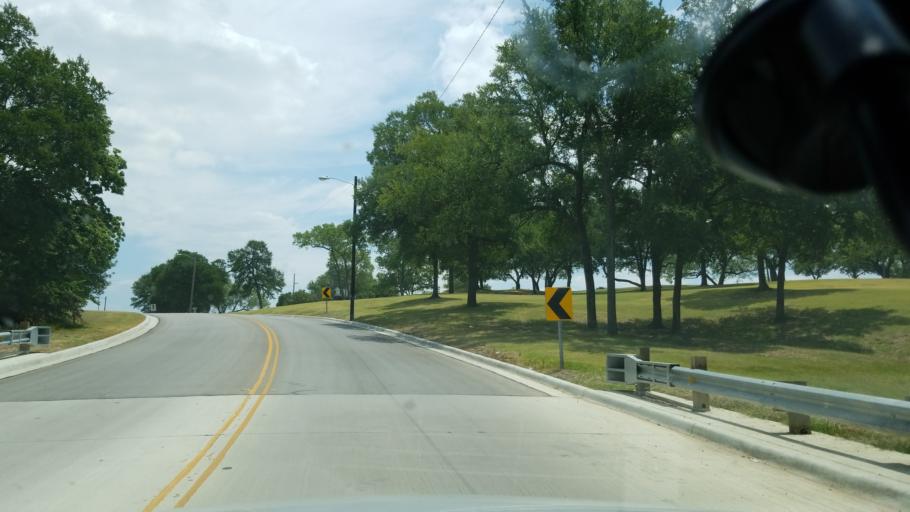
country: US
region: Texas
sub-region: Dallas County
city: Grand Prairie
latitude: 32.7552
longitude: -96.9972
